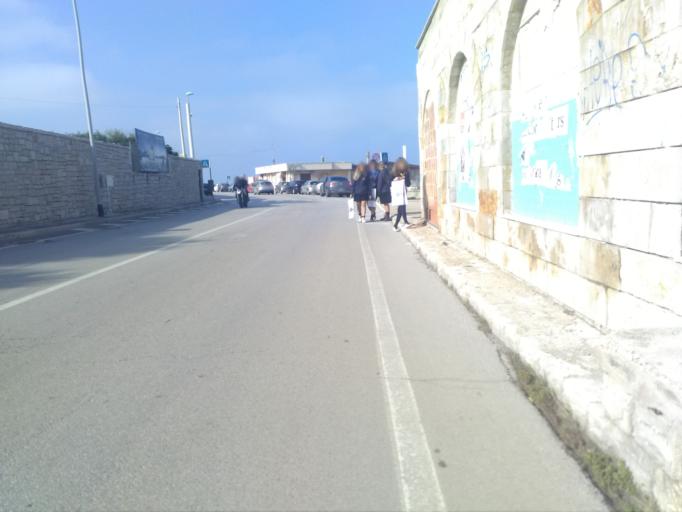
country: IT
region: Apulia
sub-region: Provincia di Bari
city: San Paolo
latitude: 41.1641
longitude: 16.7565
